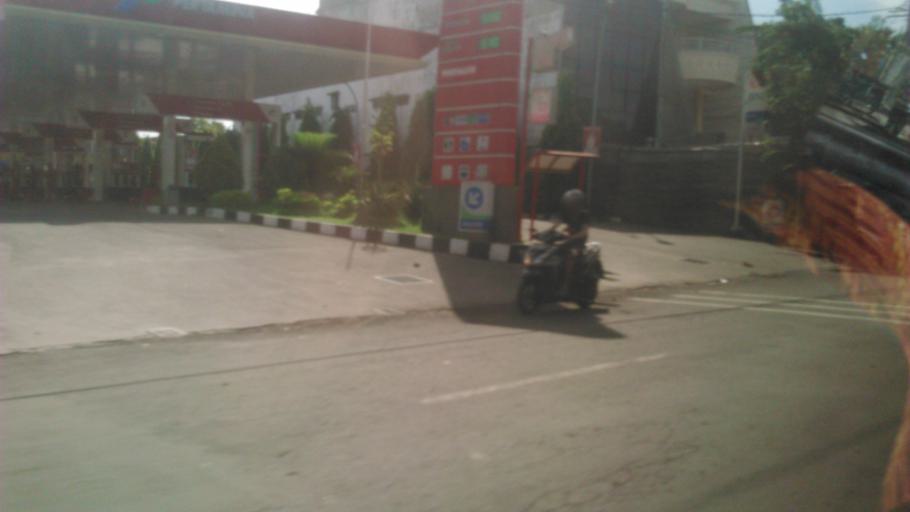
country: ID
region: East Java
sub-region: Kota Surabaya
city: Surabaya
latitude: -7.2492
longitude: 112.7546
